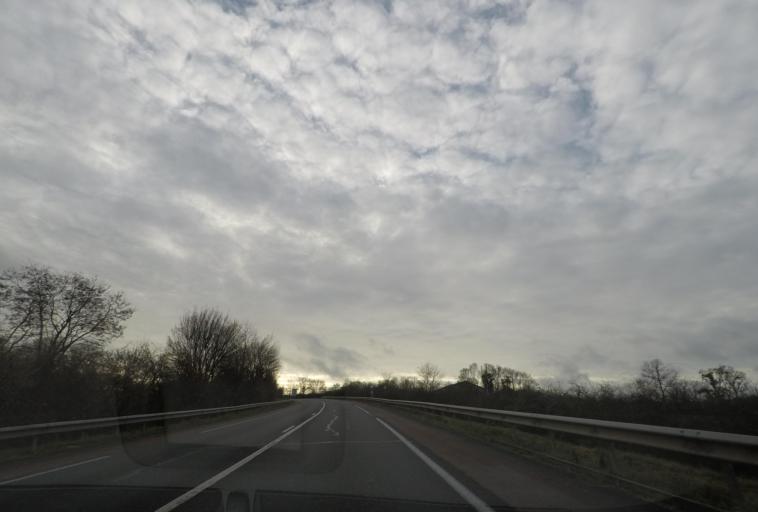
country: FR
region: Pays de la Loire
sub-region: Departement de la Sarthe
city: Saint-Calais
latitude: 47.9221
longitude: 0.7629
